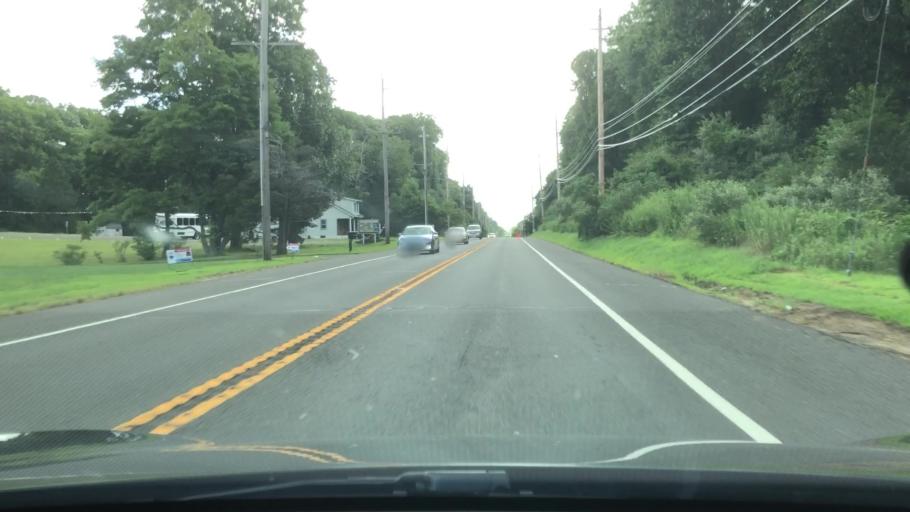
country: US
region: New Jersey
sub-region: Monmouth County
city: West Freehold
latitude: 40.2569
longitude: -74.3132
